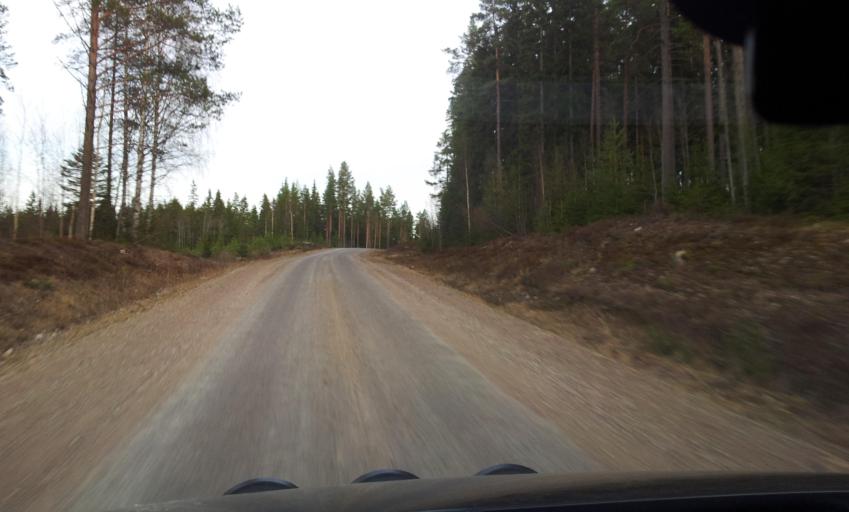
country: SE
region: Gaevleborg
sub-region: Ljusdals Kommun
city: Farila
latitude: 62.0505
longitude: 15.8198
